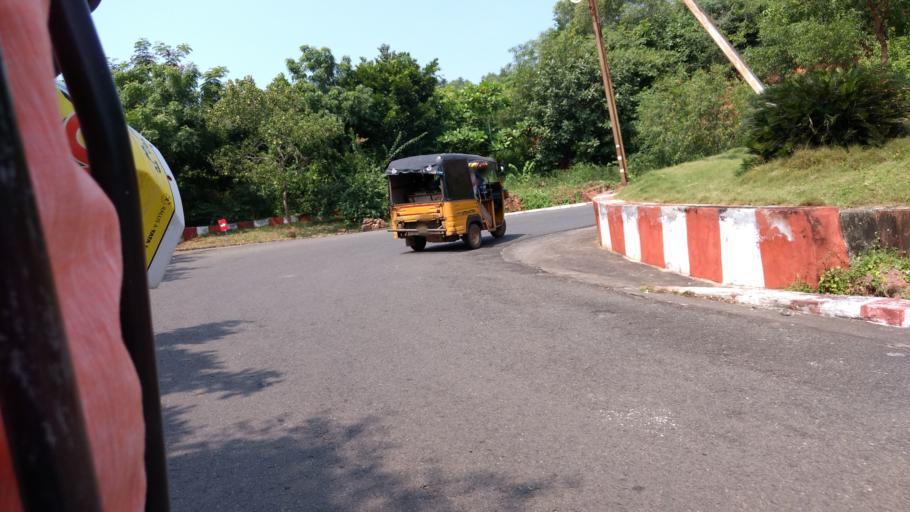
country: IN
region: Andhra Pradesh
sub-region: East Godavari
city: Tuni
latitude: 17.2799
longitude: 82.3977
